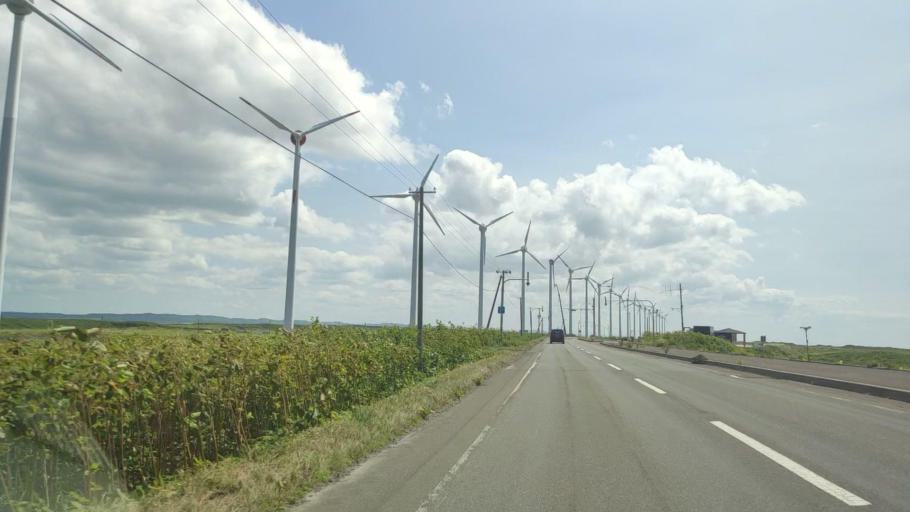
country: JP
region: Hokkaido
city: Makubetsu
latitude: 44.9765
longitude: 141.6959
